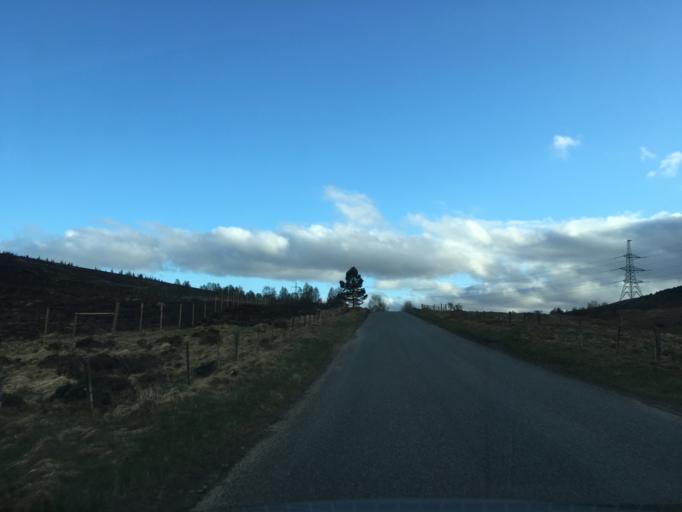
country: GB
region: Scotland
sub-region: Perth and Kinross
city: Aberfeldy
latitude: 56.7474
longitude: -4.0933
